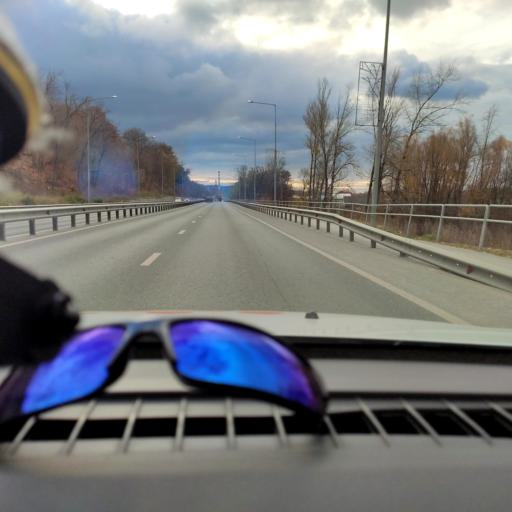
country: RU
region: Samara
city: Volzhskiy
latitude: 53.3930
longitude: 50.1560
